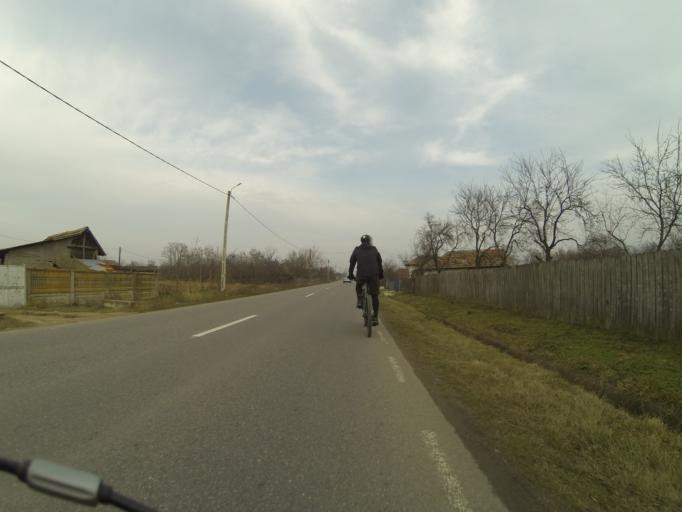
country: RO
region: Mehedinti
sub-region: Comuna Corlatel
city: Corlatel
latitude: 44.4010
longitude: 22.9344
